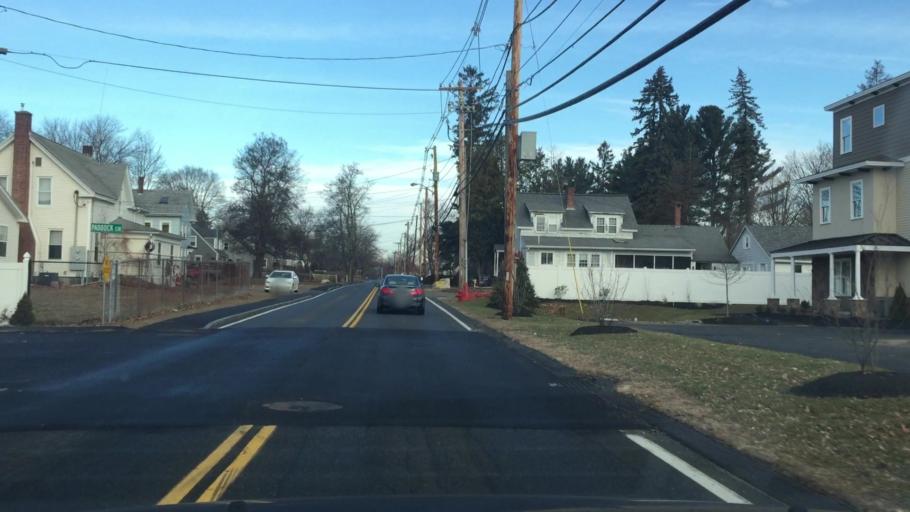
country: US
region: New Hampshire
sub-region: Rockingham County
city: Salem
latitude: 42.7784
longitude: -71.2312
